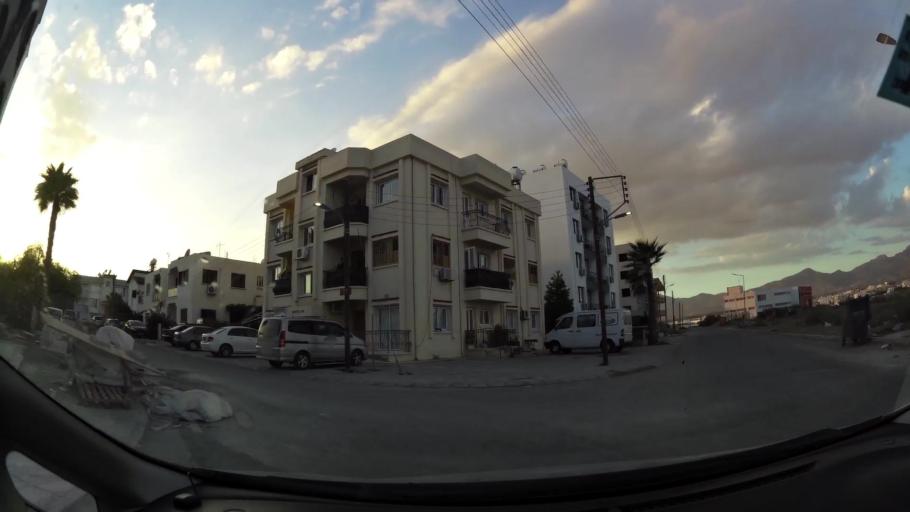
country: CY
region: Lefkosia
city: Nicosia
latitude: 35.2011
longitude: 33.3726
